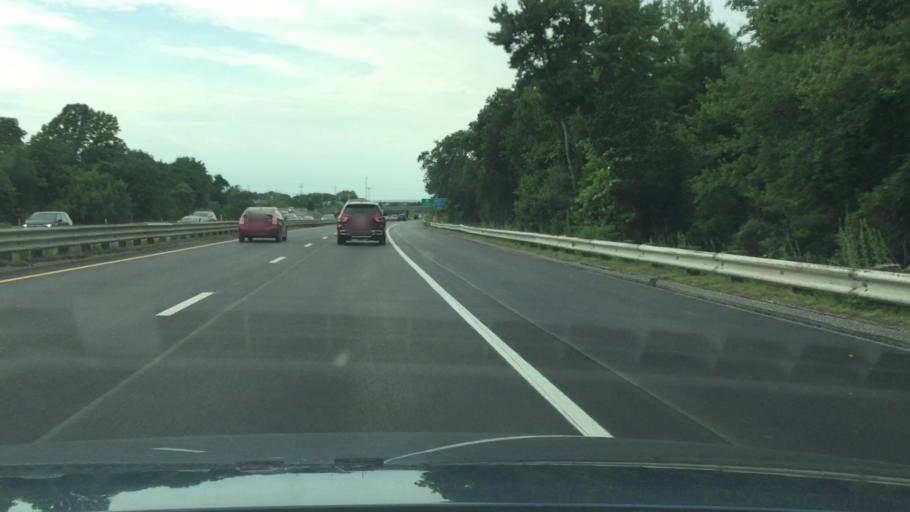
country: US
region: Massachusetts
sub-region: Plymouth County
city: Kingston
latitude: 41.9843
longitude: -70.7167
